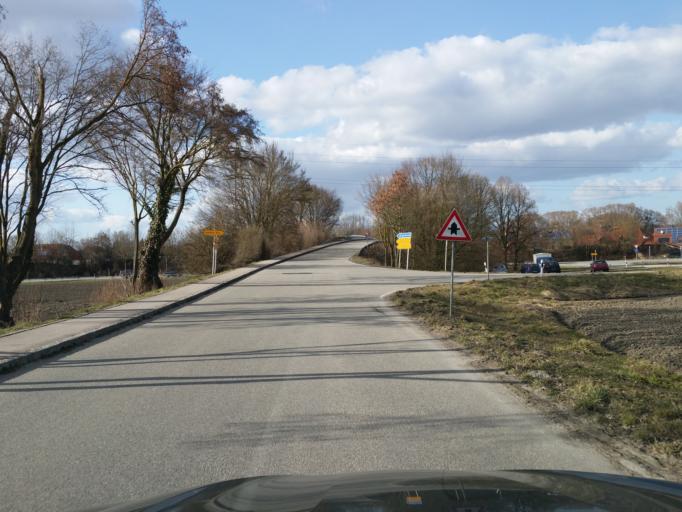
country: DE
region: Bavaria
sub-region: Lower Bavaria
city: Eching
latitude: 48.4948
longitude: 12.0392
